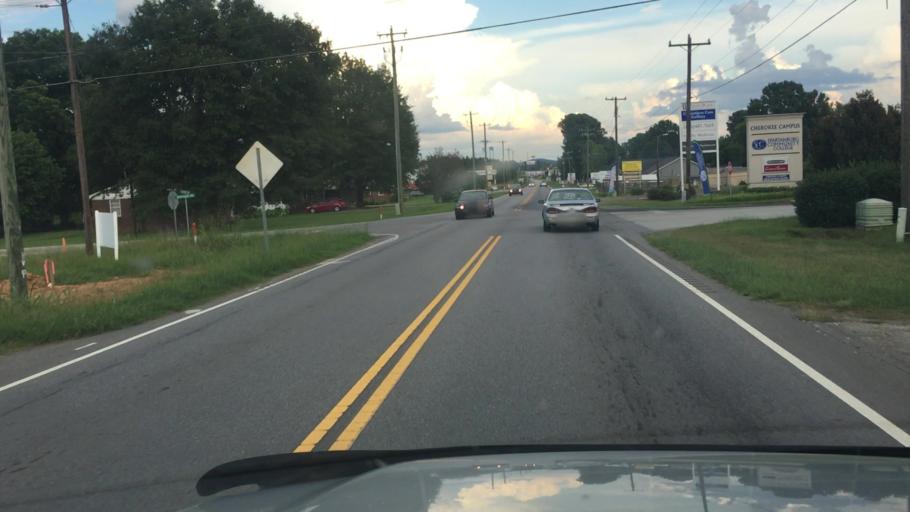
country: US
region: South Carolina
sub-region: Cherokee County
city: Gaffney
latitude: 35.1028
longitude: -81.6796
